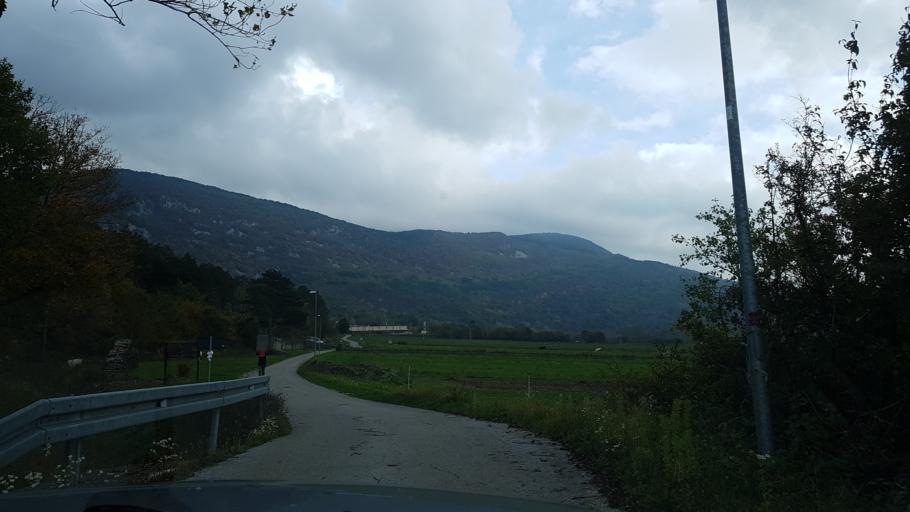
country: HR
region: Istarska
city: Buzet
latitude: 45.4088
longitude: 14.1070
